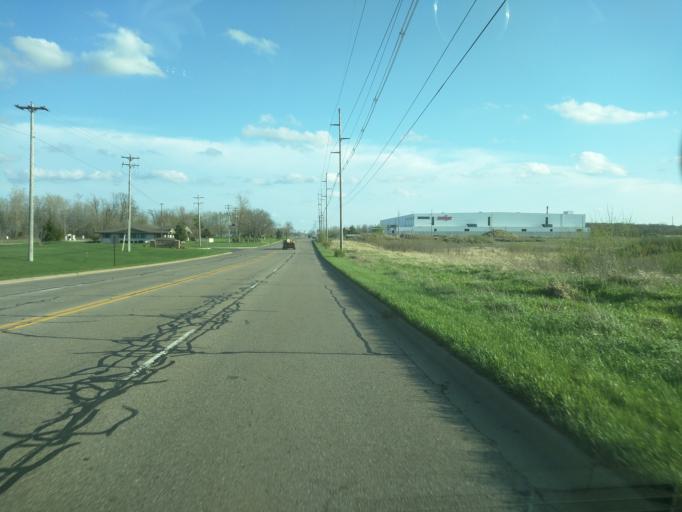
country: US
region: Michigan
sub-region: Eaton County
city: Waverly
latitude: 42.7165
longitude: -84.6426
